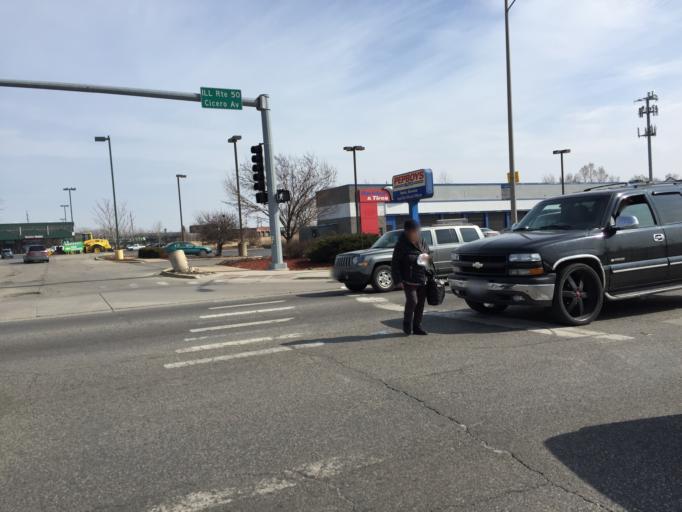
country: US
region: Illinois
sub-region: Cook County
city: Cicero
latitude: 41.8466
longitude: -87.7442
